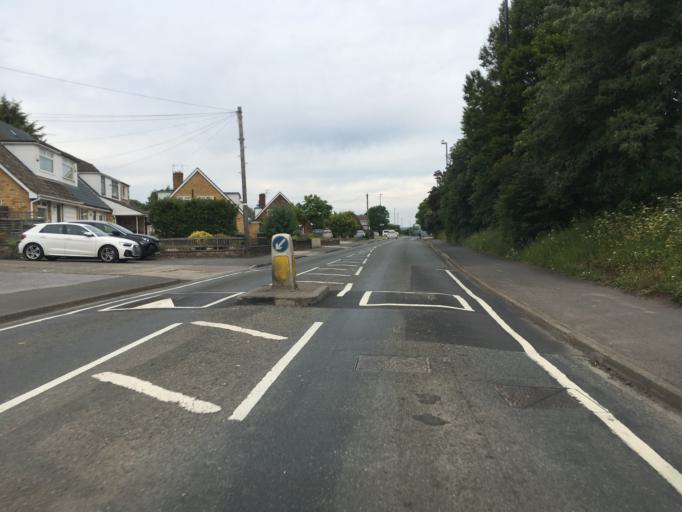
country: GB
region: England
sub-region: Bath and North East Somerset
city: Whitchurch
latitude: 51.4079
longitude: -2.5789
